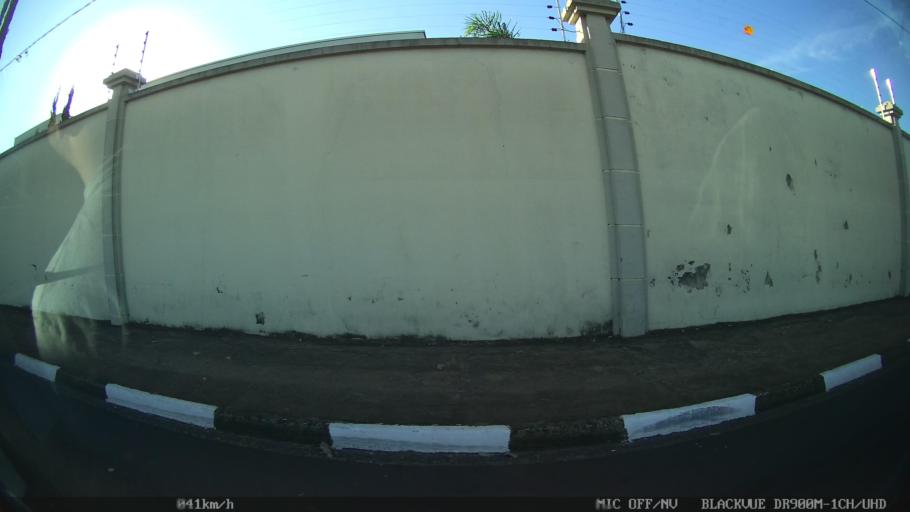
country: BR
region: Sao Paulo
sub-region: Franca
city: Franca
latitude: -20.5146
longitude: -47.3759
